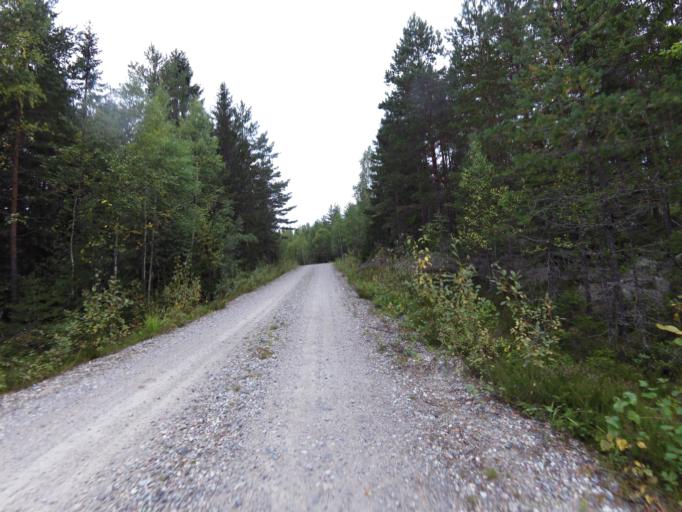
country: SE
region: Gaevleborg
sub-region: Gavle Kommun
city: Valbo
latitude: 60.7361
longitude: 17.0251
